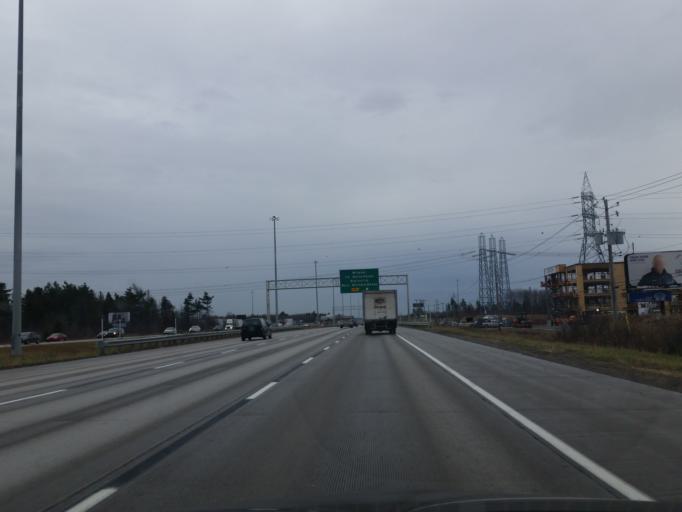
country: CA
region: Quebec
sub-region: Laurentides
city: Blainville
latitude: 45.6836
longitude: -73.9238
